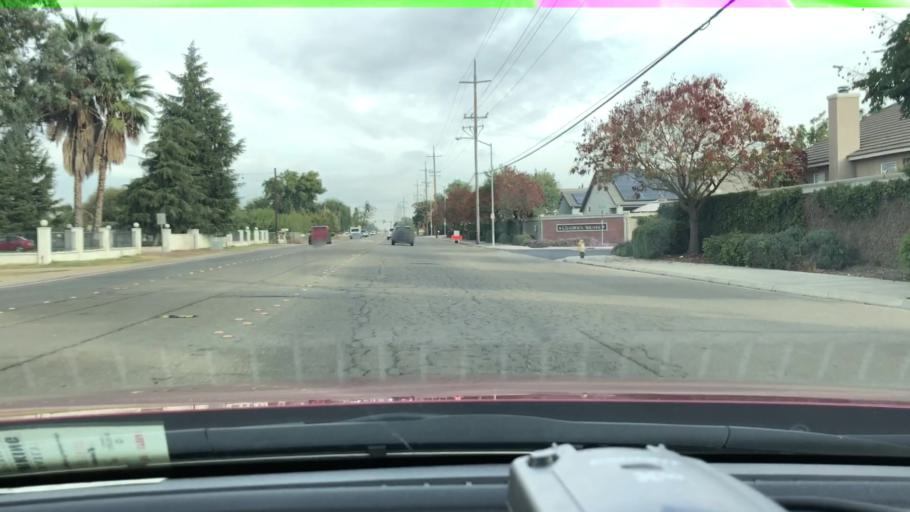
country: US
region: California
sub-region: San Joaquin County
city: Lathrop
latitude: 37.8224
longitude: -121.2536
